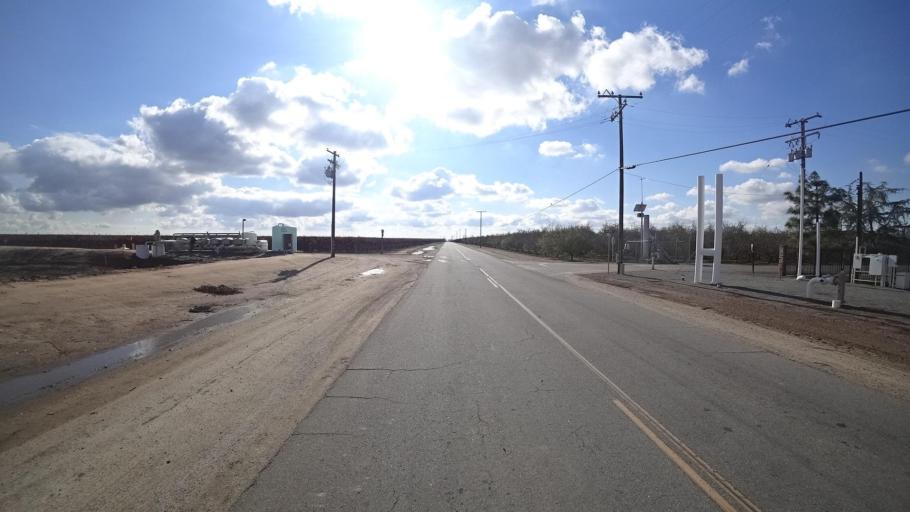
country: US
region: California
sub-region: Kern County
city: McFarland
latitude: 35.6675
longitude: -119.2047
